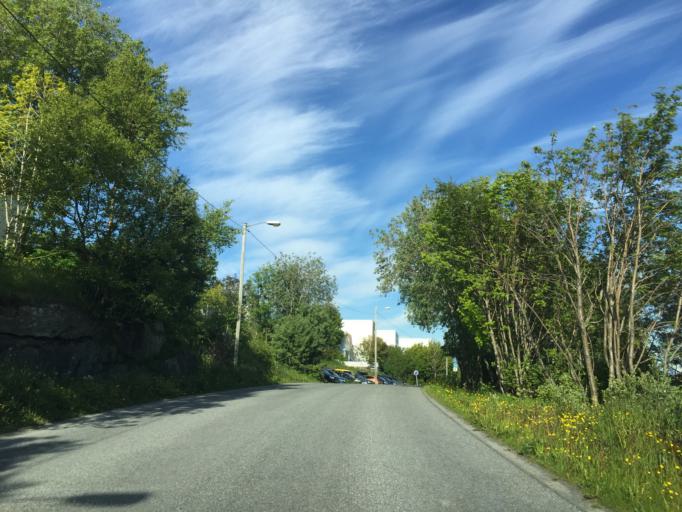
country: NO
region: Nordland
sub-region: Bodo
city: Lopsmarka
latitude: 67.2812
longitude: 14.5330
